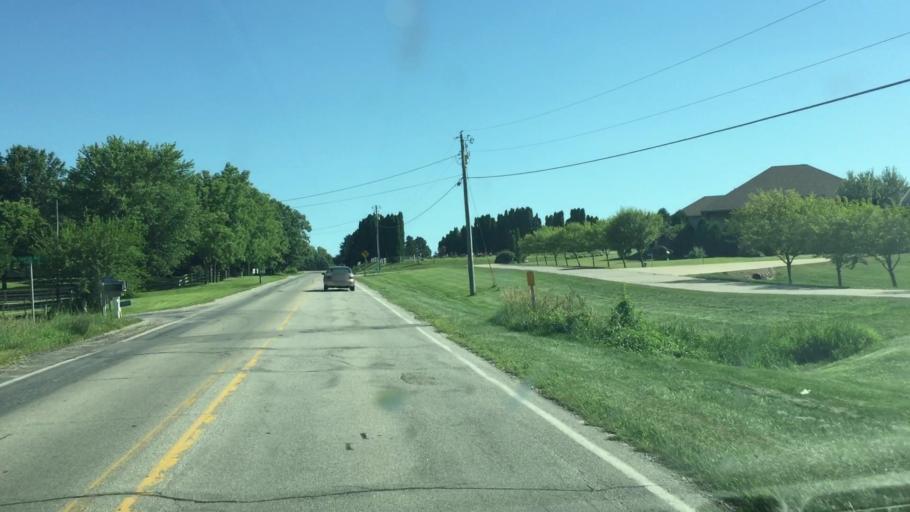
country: US
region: Iowa
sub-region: Linn County
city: Ely
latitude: 41.8459
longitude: -91.6461
